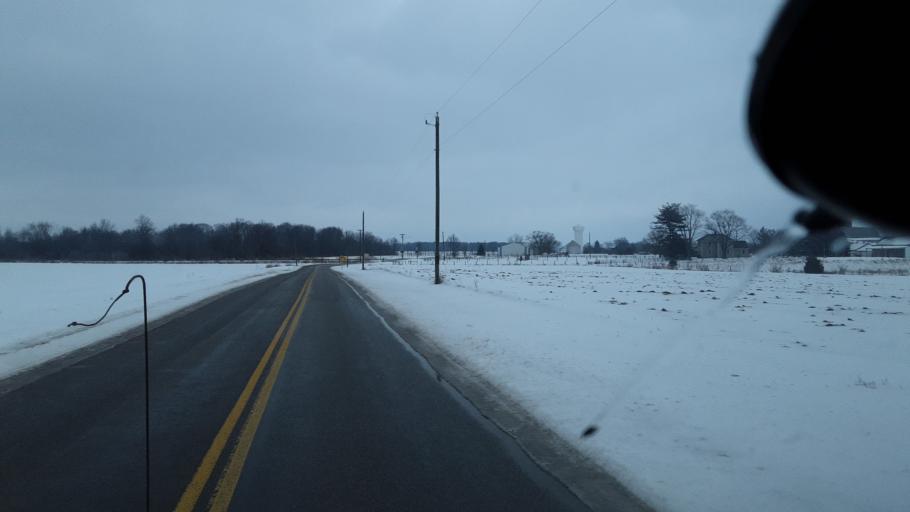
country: US
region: Ohio
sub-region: Union County
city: New California
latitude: 40.1845
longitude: -83.3021
